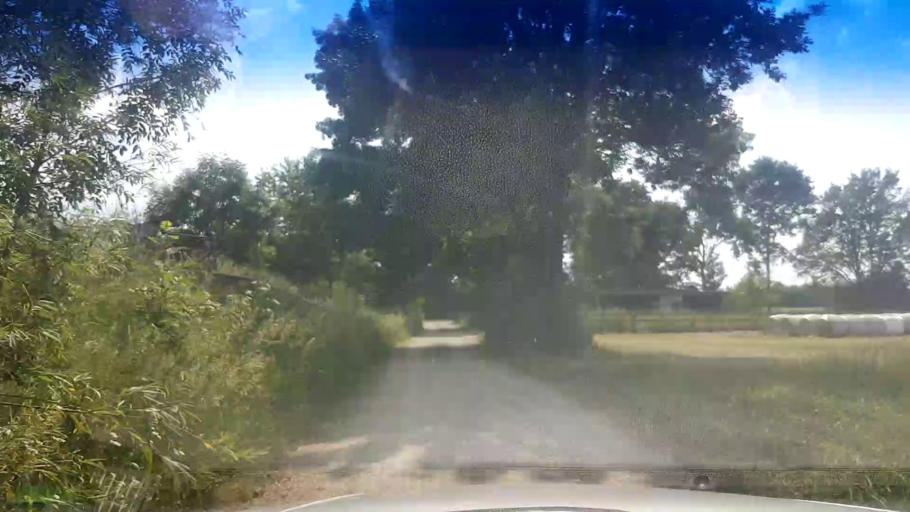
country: DE
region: Bavaria
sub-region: Upper Franconia
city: Rattelsdorf
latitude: 50.0024
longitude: 10.9018
